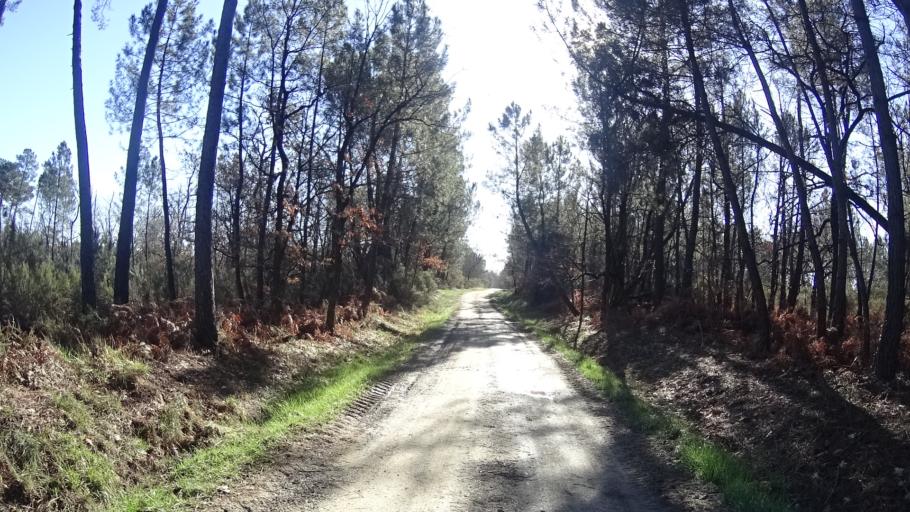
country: FR
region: Aquitaine
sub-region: Departement de la Dordogne
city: La Roche-Chalais
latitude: 45.1679
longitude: 0.0395
